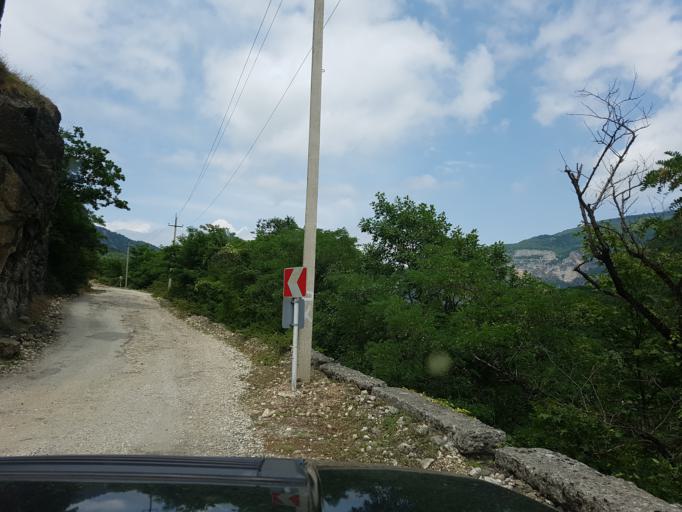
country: GE
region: Imereti
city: Tsqaltubo
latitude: 42.4915
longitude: 42.7843
